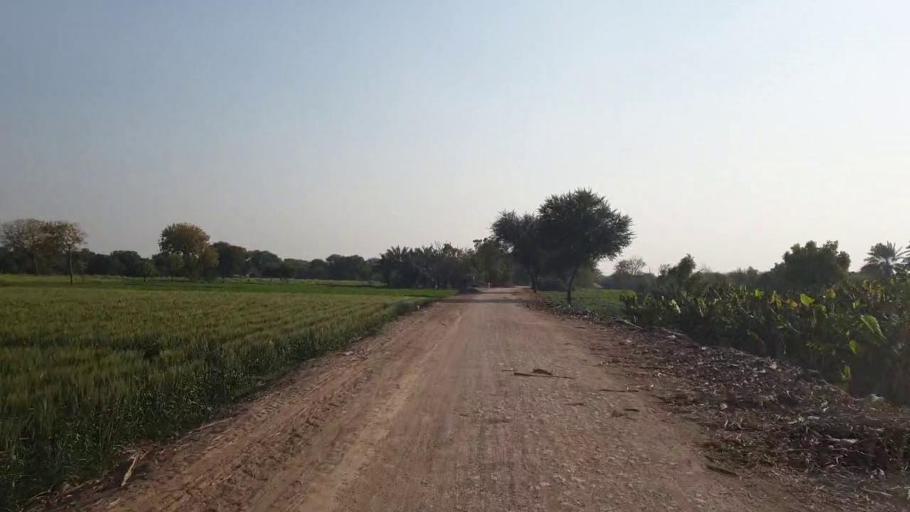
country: PK
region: Sindh
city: Mirpur Khas
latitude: 25.4114
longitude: 68.9439
